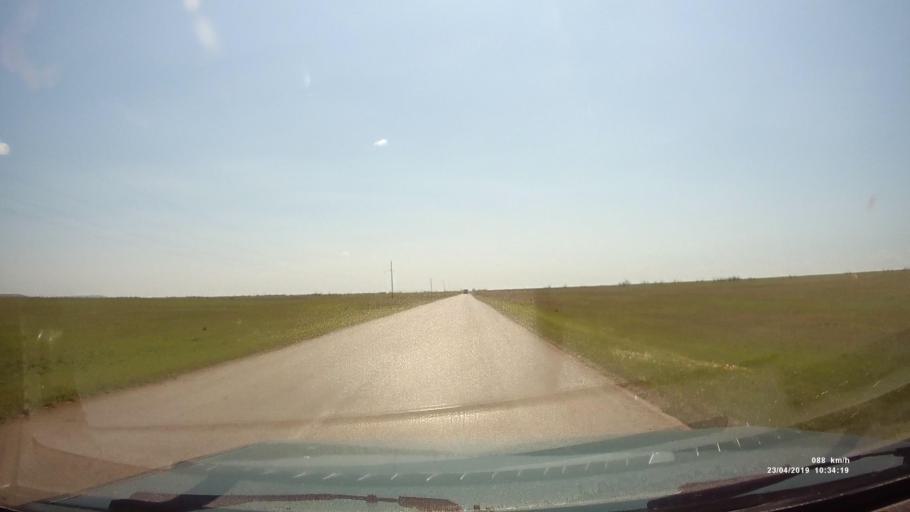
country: RU
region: Kalmykiya
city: Yashalta
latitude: 46.5651
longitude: 42.6088
